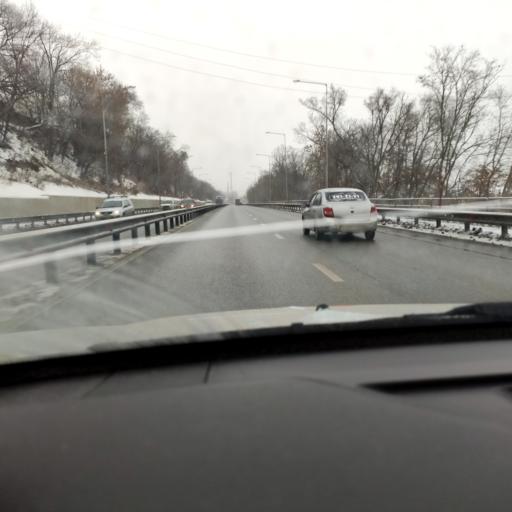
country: RU
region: Samara
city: Volzhskiy
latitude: 53.3925
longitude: 50.1562
